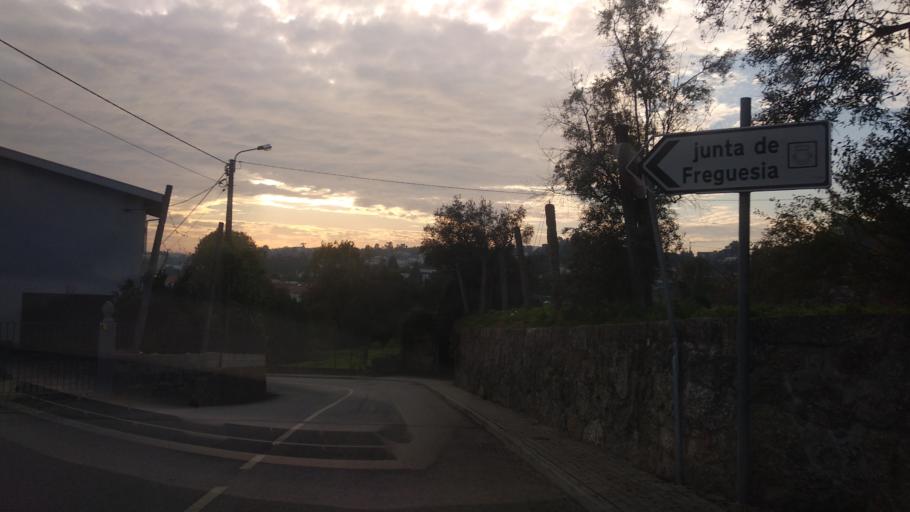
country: PT
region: Braga
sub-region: Braga
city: Braga
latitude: 41.5254
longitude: -8.4575
